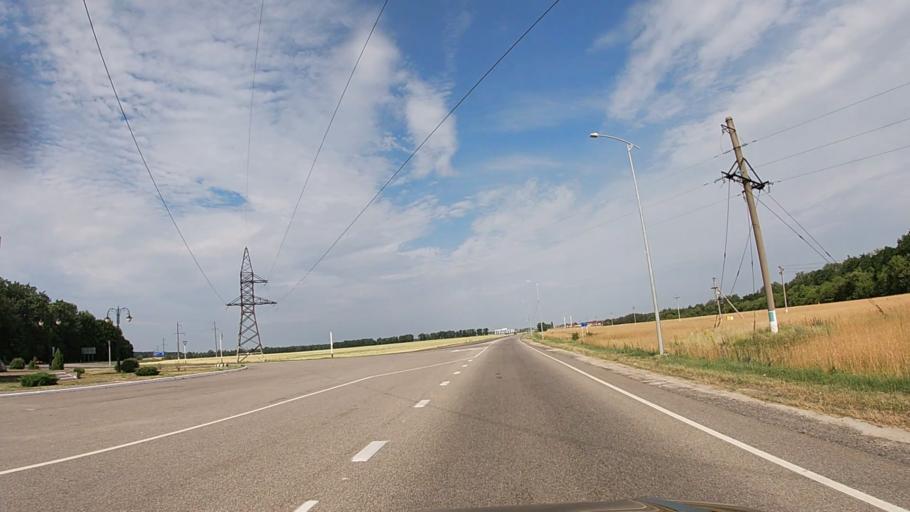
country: RU
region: Belgorod
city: Krasnaya Yaruga
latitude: 50.7962
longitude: 35.7105
